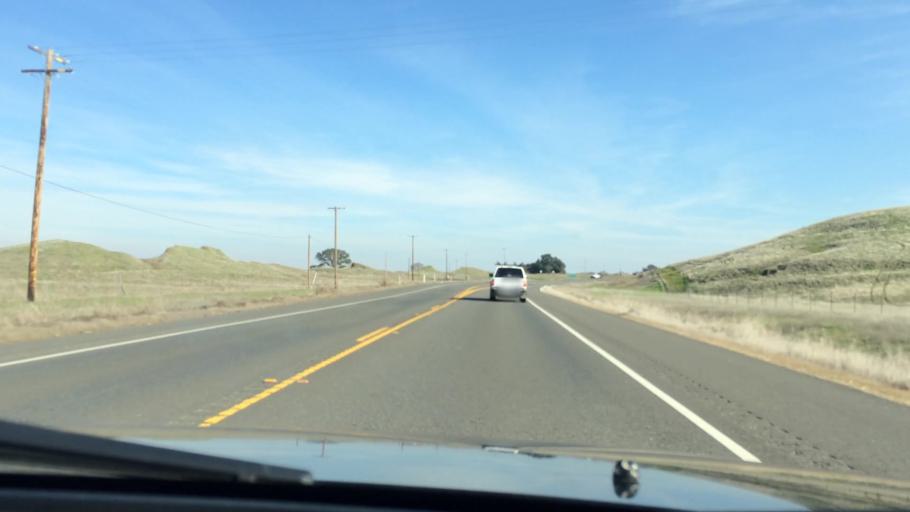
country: US
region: California
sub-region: Sacramento County
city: Rancho Murieta
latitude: 38.4859
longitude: -121.0571
